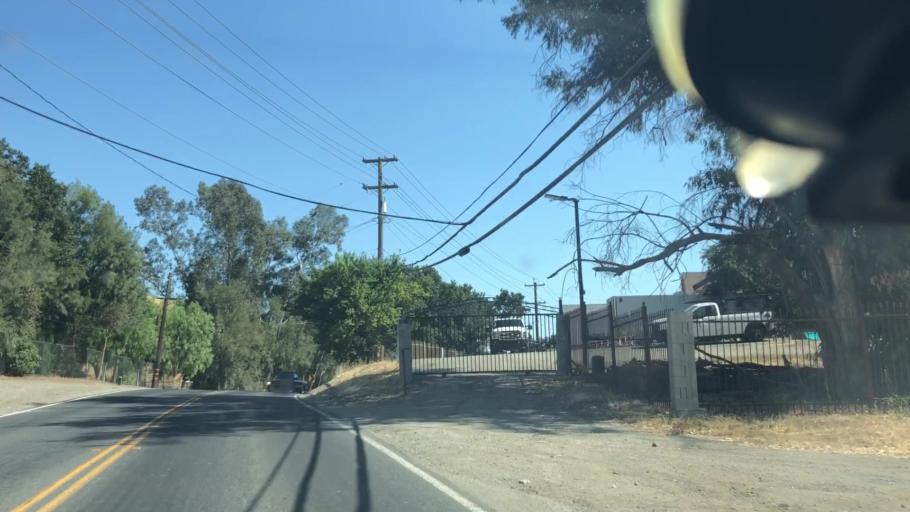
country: US
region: California
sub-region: Alameda County
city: Dublin
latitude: 37.7415
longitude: -121.8710
